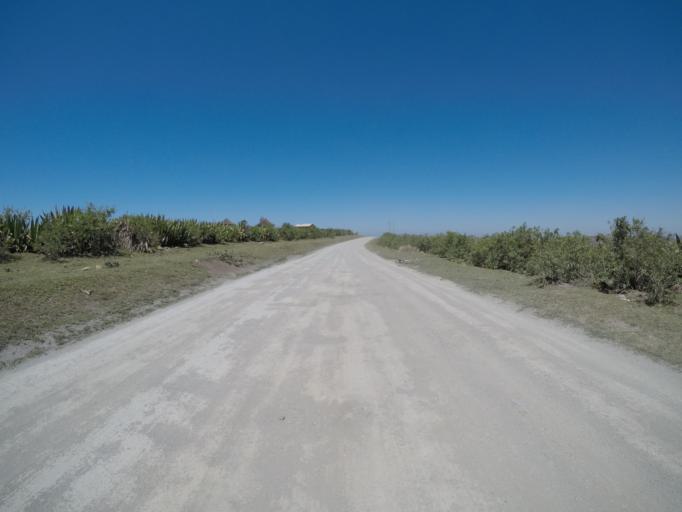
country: ZA
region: Eastern Cape
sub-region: OR Tambo District Municipality
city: Libode
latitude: -32.0075
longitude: 29.0736
